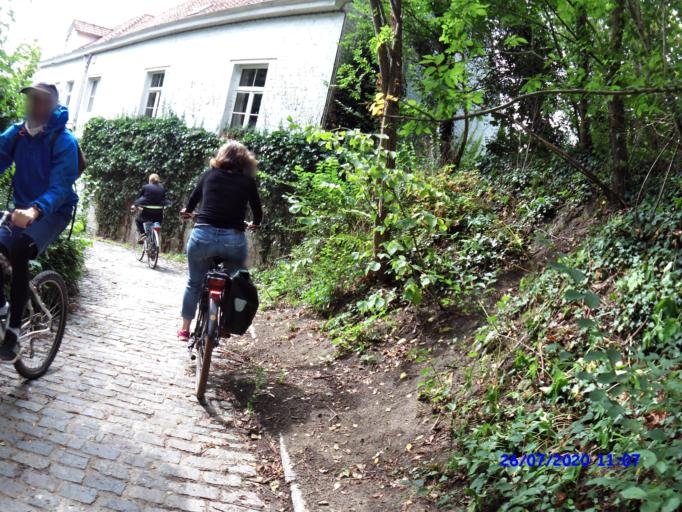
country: BE
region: Flanders
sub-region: Provincie Vlaams-Brabant
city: Linkebeek
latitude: 50.7740
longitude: 4.3540
